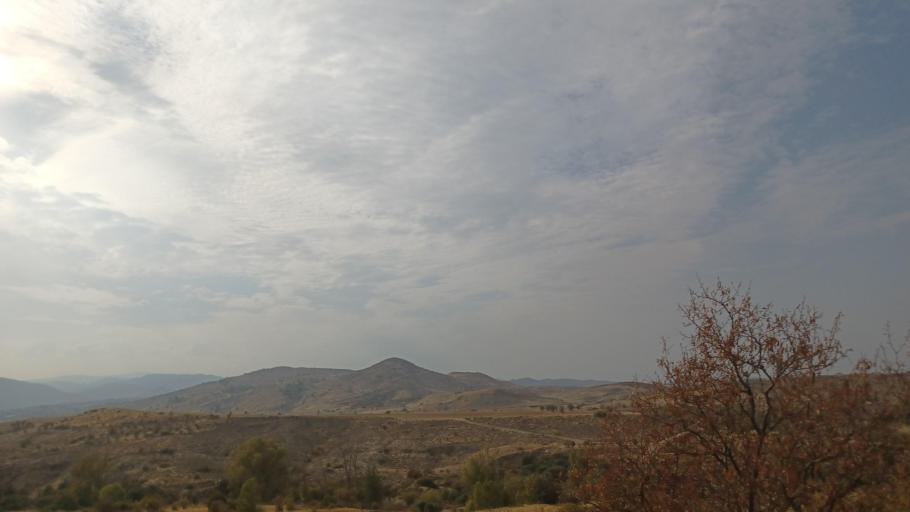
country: CY
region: Lefkosia
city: Peristerona
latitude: 35.0713
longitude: 33.0913
